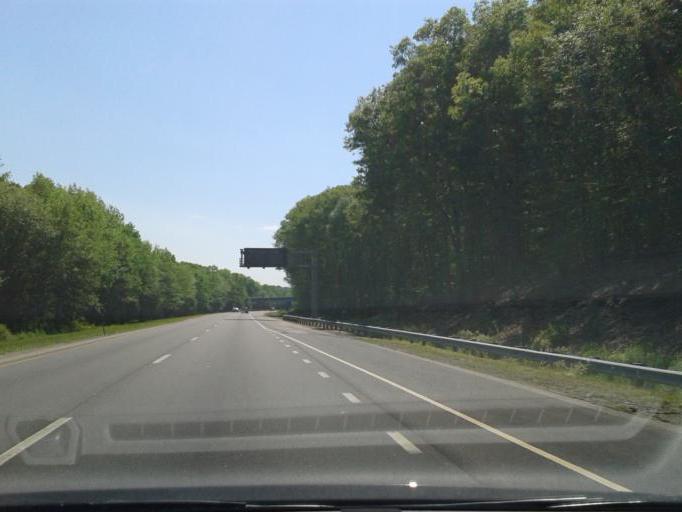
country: US
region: Rhode Island
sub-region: Washington County
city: Ashaway
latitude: 41.4341
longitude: -71.8104
